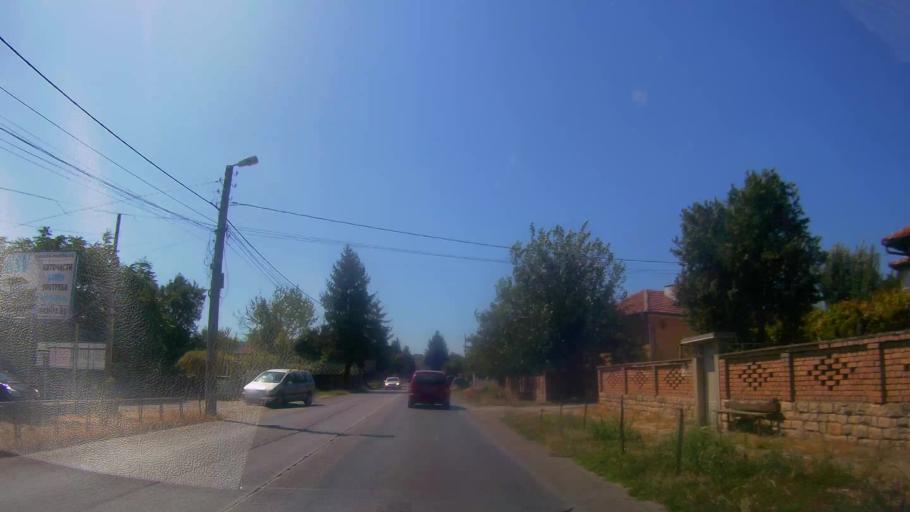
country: BG
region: Veliko Turnovo
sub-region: Obshtina Gorna Oryakhovitsa
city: Purvomaytsi
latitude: 43.1464
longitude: 25.6132
